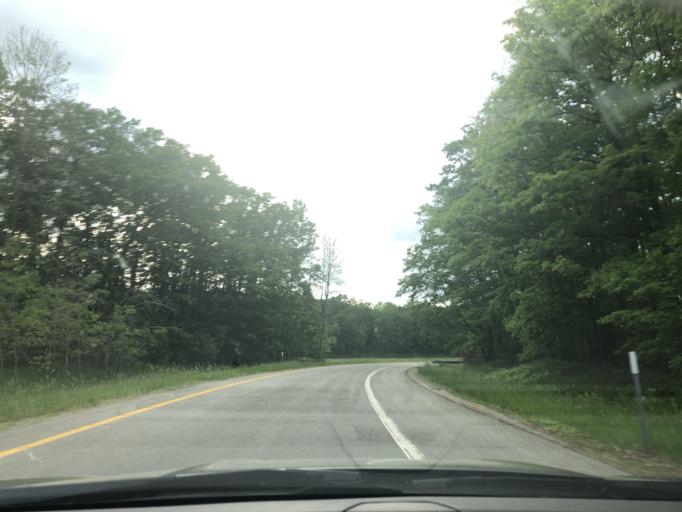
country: US
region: Michigan
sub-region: Clare County
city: Harrison
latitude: 43.9924
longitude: -84.7746
